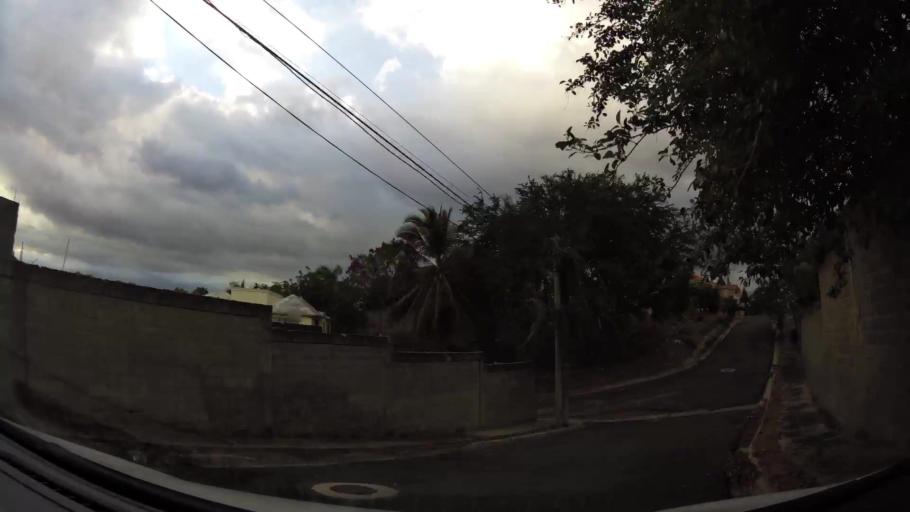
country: DO
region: Nacional
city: Santo Domingo
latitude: 18.4990
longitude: -69.9699
